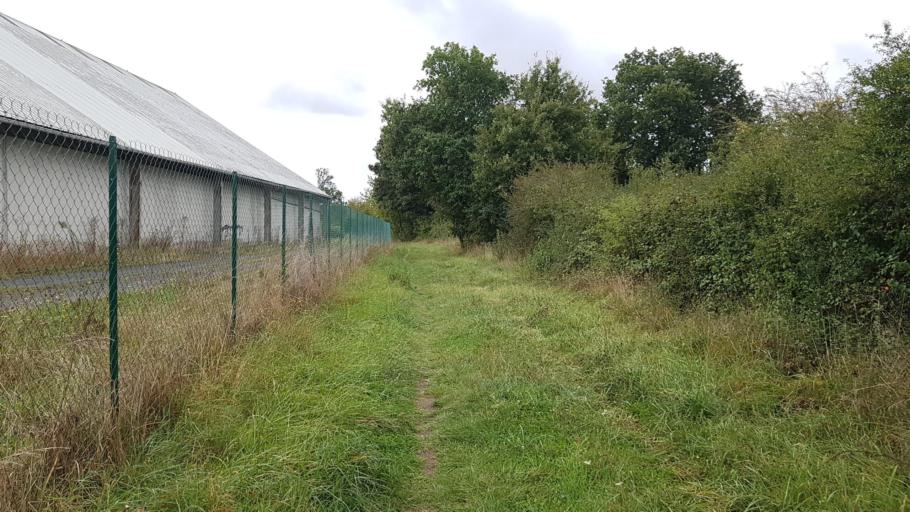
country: FR
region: Poitou-Charentes
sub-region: Departement de la Vienne
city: Saint-Savin
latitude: 46.5636
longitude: 0.8600
